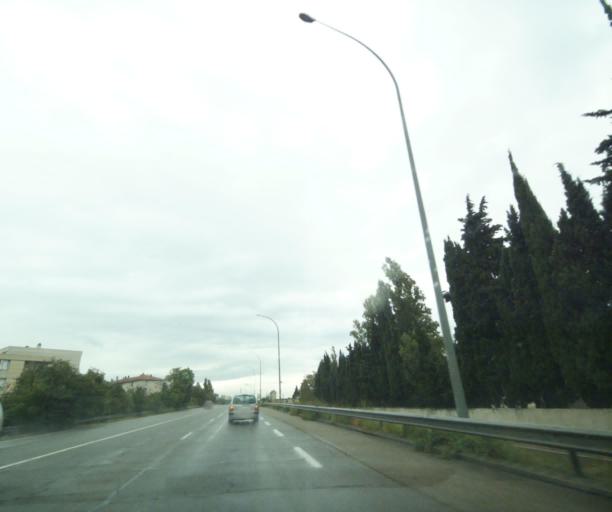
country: FR
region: Languedoc-Roussillon
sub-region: Departement du Gard
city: Rodilhan
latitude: 43.8447
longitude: 4.3938
